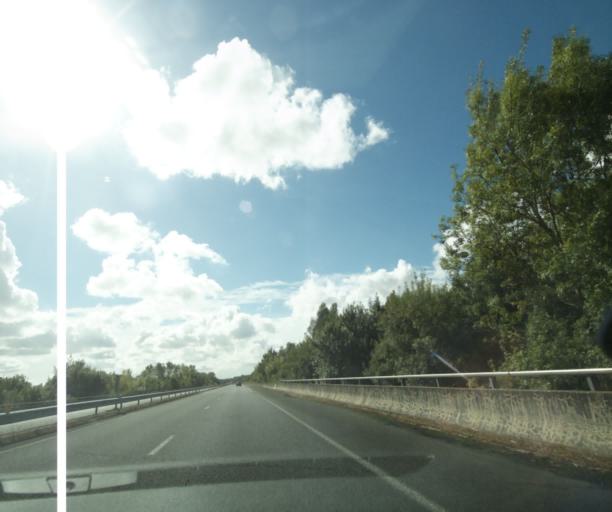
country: FR
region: Poitou-Charentes
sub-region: Departement de la Charente-Maritime
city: Saint-Savinien
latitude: 45.8679
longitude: -0.7329
